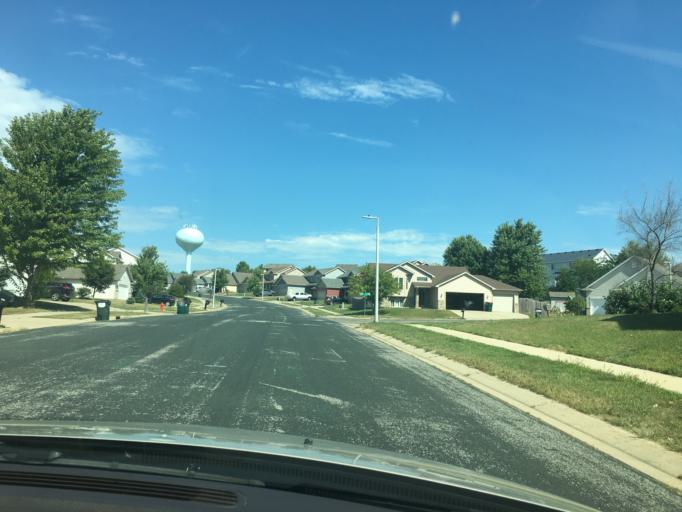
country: US
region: Minnesota
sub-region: Olmsted County
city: Oronoco
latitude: 44.0876
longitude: -92.5255
